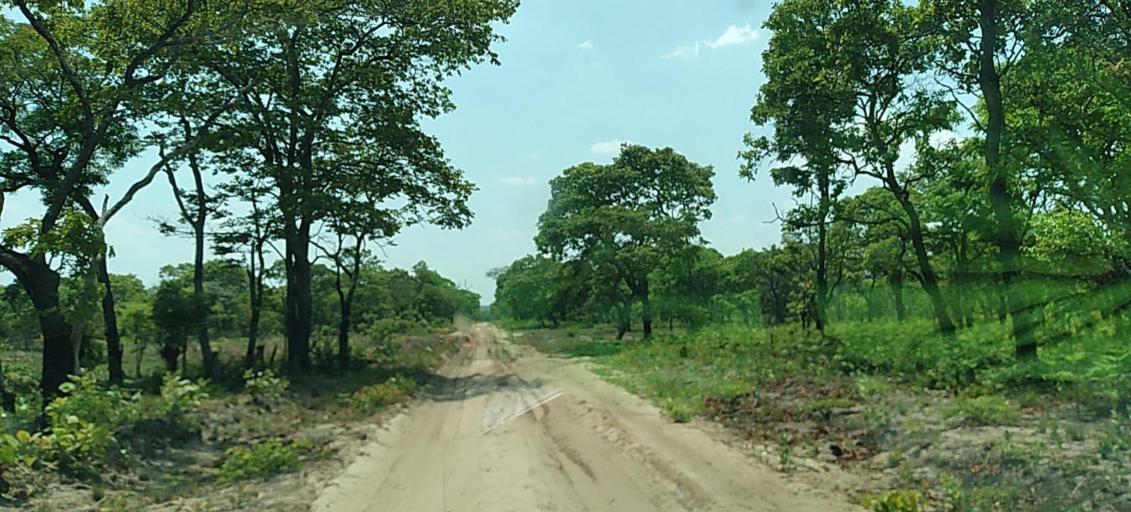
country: CD
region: Katanga
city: Kolwezi
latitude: -11.3031
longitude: 25.2314
